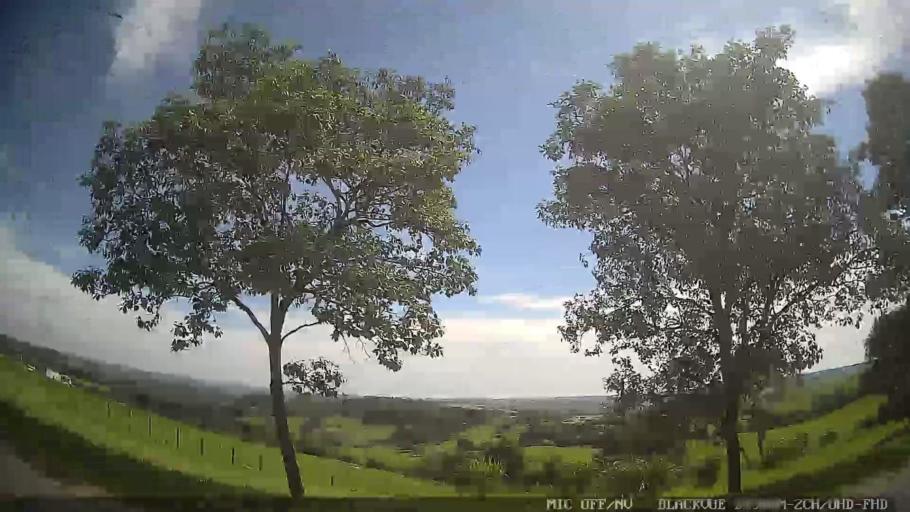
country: BR
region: Sao Paulo
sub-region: Porto Feliz
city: Porto Feliz
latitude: -23.1974
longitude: -47.6150
